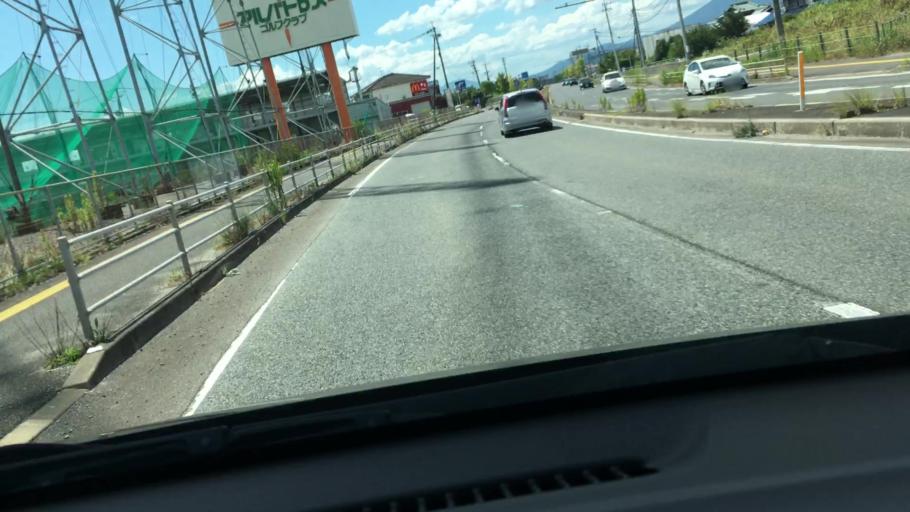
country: JP
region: Saga Prefecture
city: Saga-shi
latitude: 33.2737
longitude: 130.3344
